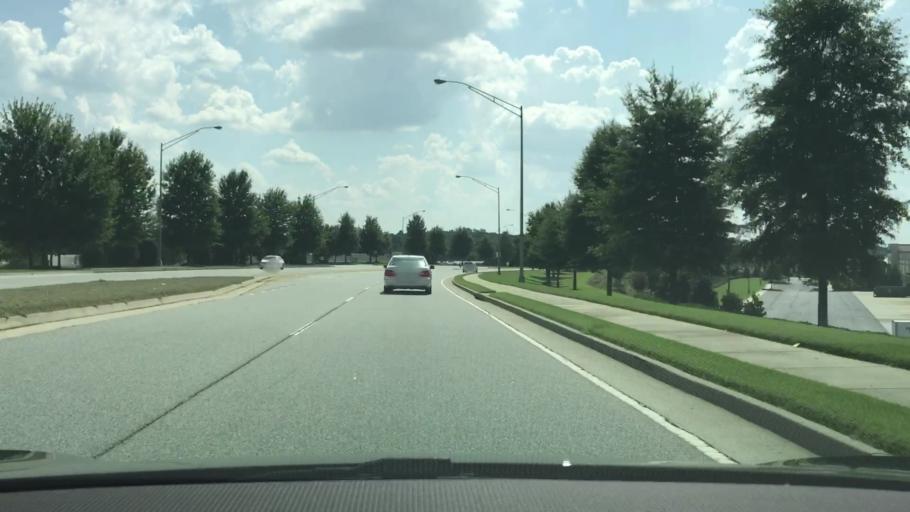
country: US
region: Georgia
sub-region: Gwinnett County
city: Sugar Hill
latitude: 34.0808
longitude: -84.0050
